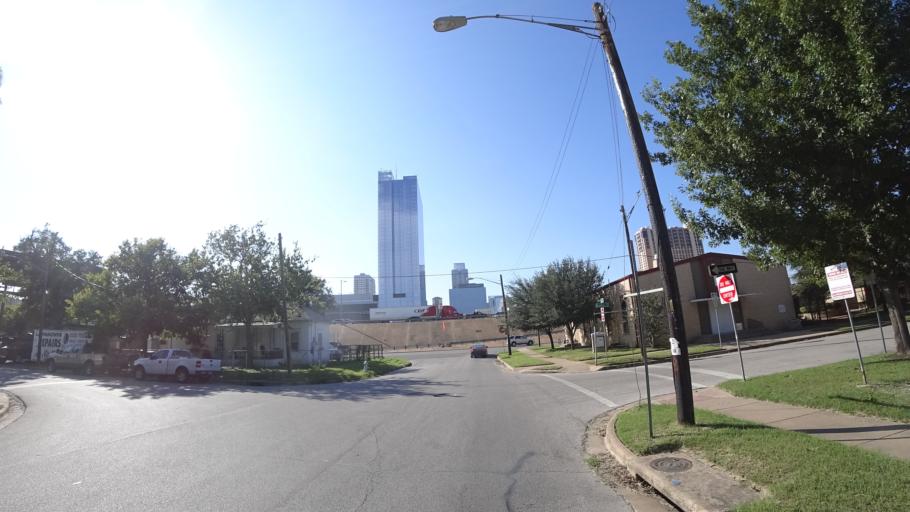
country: US
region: Texas
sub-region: Travis County
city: Austin
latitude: 30.2618
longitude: -97.7350
